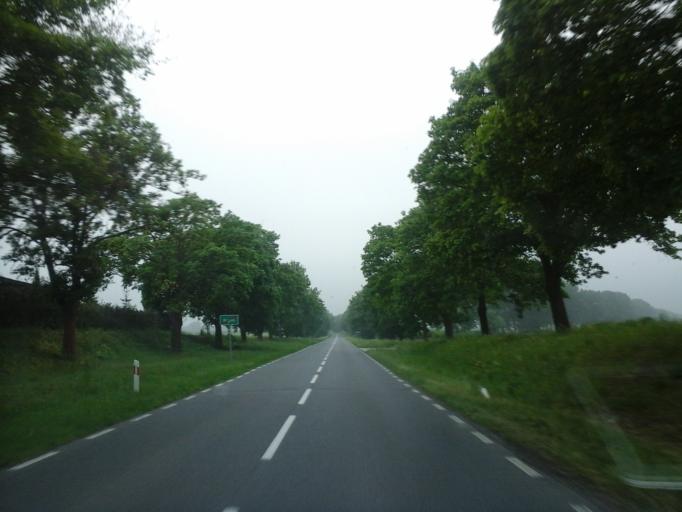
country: PL
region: West Pomeranian Voivodeship
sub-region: Powiat choszczenski
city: Choszczno
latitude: 53.1566
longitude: 15.3898
